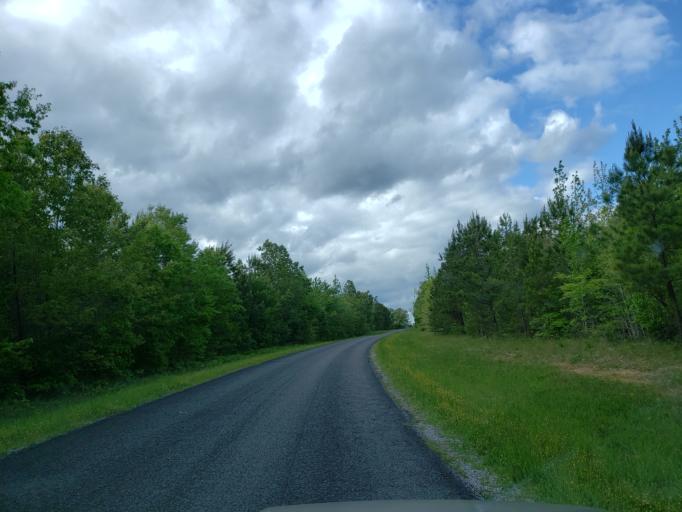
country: US
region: Georgia
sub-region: Haralson County
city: Tallapoosa
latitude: 33.8117
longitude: -85.3870
